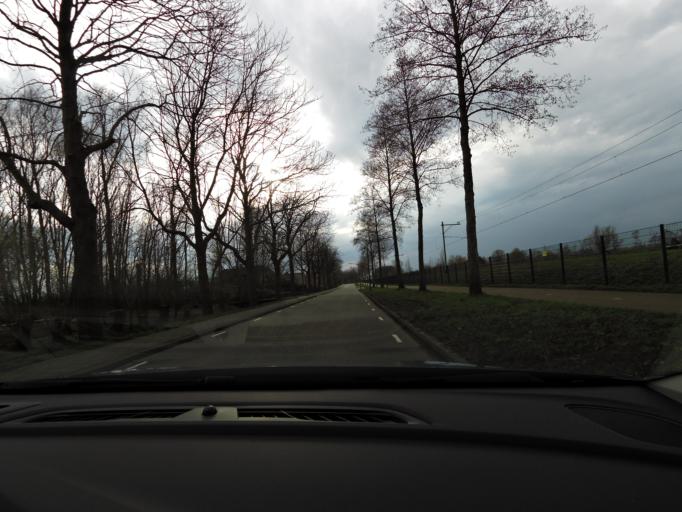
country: NL
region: South Holland
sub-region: Gemeente Hardinxveld-Giessendam
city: Neder-Hardinxveld
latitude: 51.8316
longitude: 4.8669
